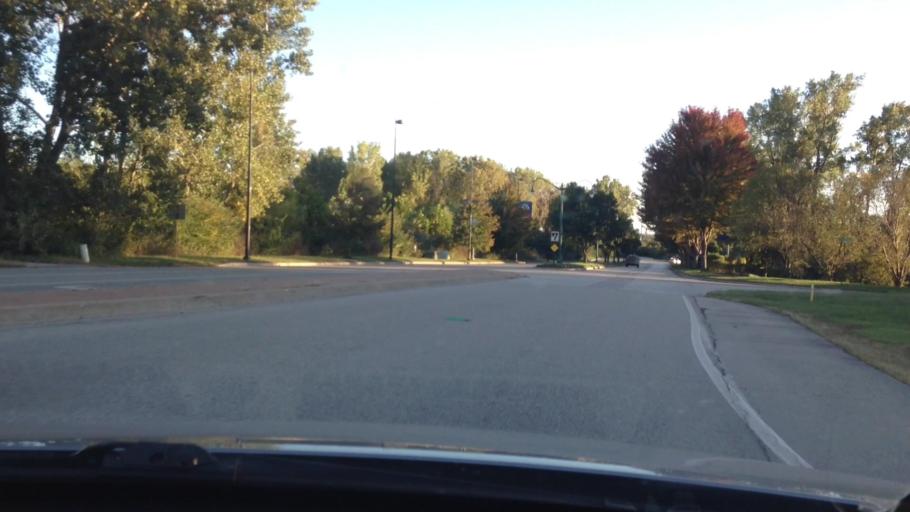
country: US
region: Missouri
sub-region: Clay County
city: Claycomo
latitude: 39.1545
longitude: -94.4773
